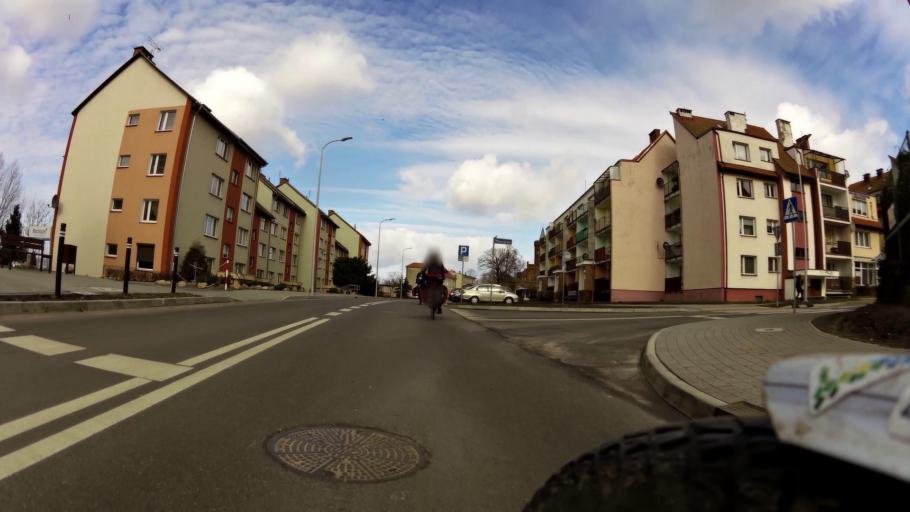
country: PL
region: West Pomeranian Voivodeship
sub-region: Powiat kamienski
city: Kamien Pomorski
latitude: 53.9701
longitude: 14.7658
